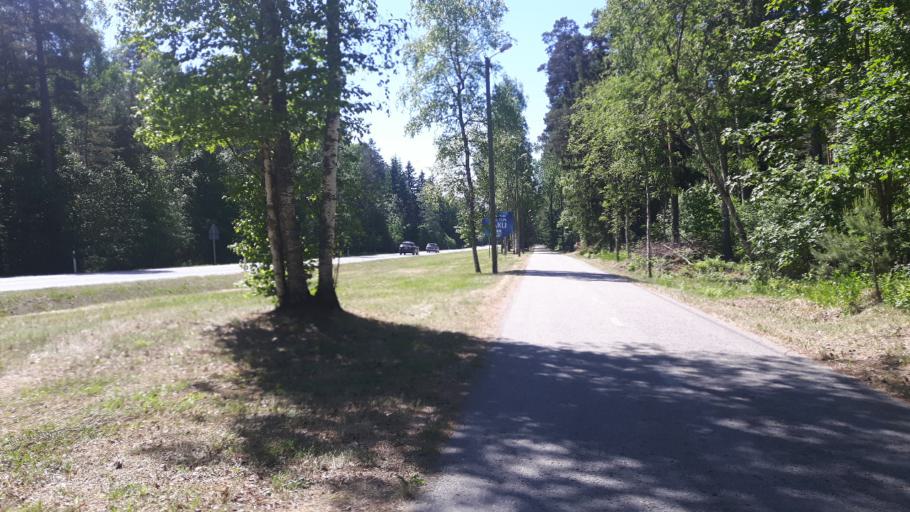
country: EE
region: Harju
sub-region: Saku vald
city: Saku
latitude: 59.3091
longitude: 24.6774
